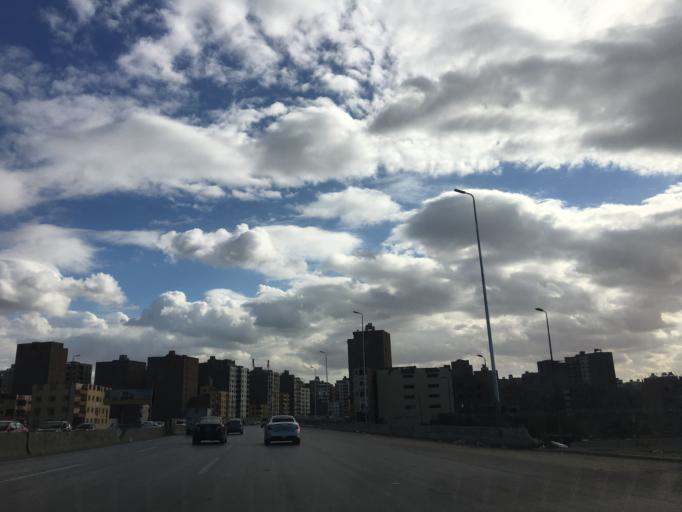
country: EG
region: Al Jizah
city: Al Jizah
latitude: 30.0233
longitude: 31.1651
